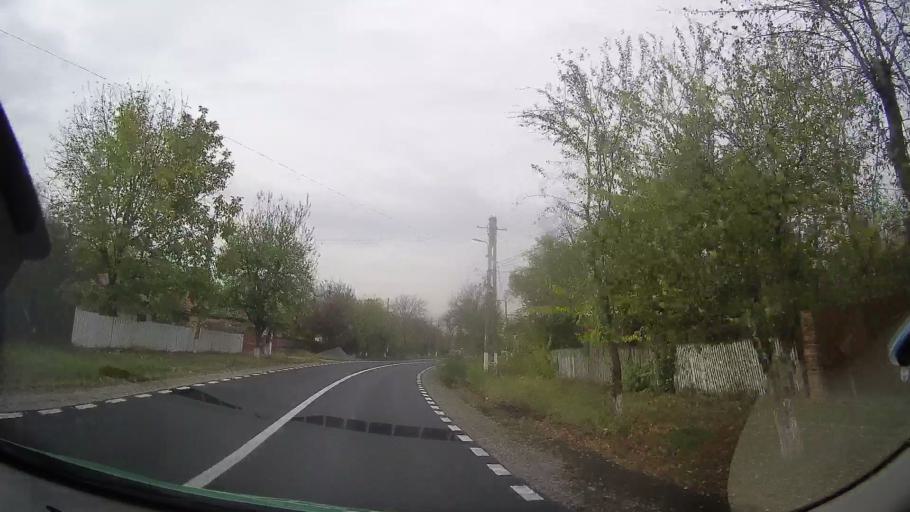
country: RO
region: Ilfov
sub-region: Comuna Nuci
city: Nuci
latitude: 44.7198
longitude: 26.3050
